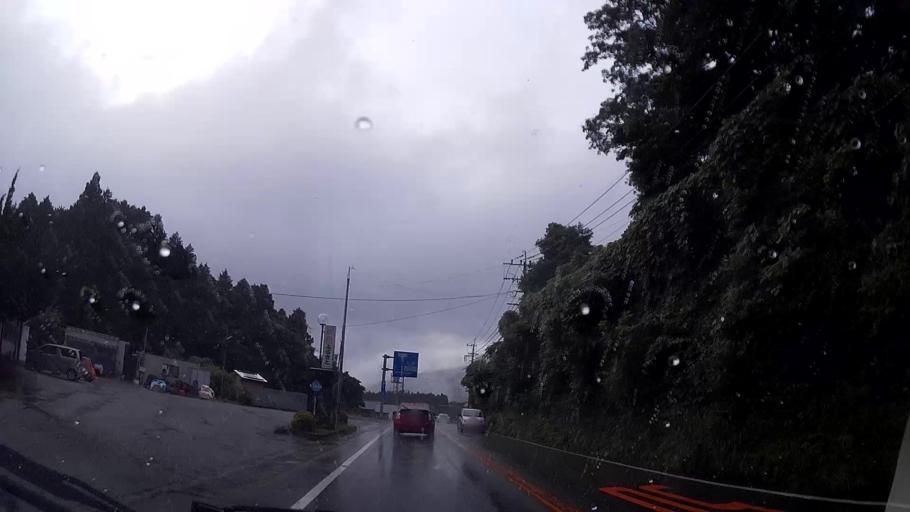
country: JP
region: Kumamoto
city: Aso
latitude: 32.8701
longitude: 130.9962
